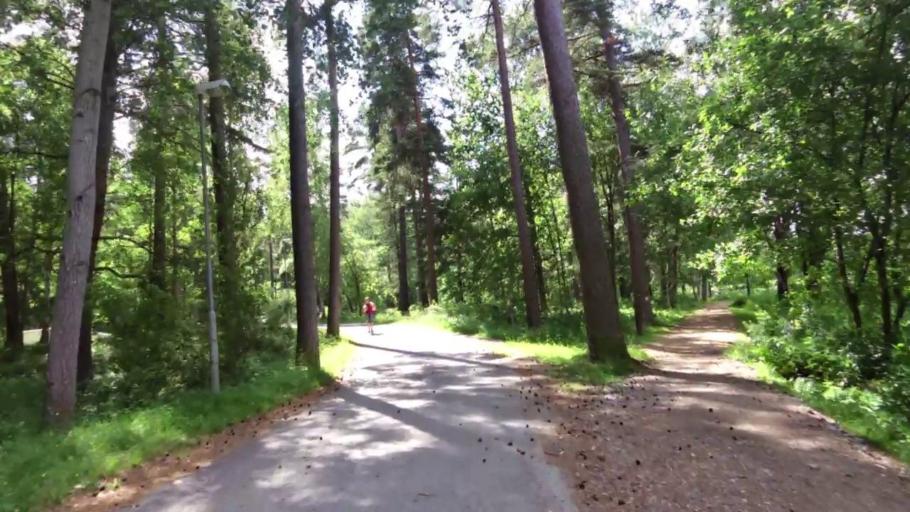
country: SE
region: OEstergoetland
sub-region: Linkopings Kommun
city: Linkoping
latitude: 58.4126
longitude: 15.5846
